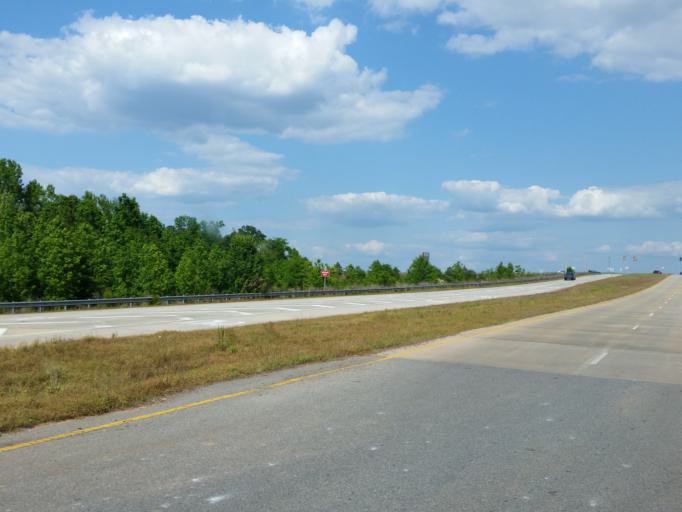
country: US
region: Georgia
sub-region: Peach County
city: Byron
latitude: 32.5864
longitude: -83.7483
